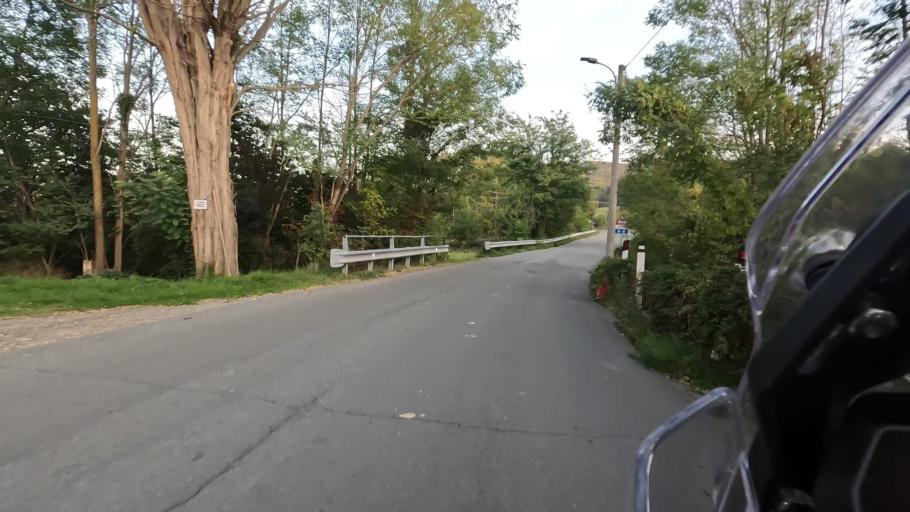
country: IT
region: Liguria
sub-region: Provincia di Savona
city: Mioglia
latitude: 44.4699
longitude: 8.4182
